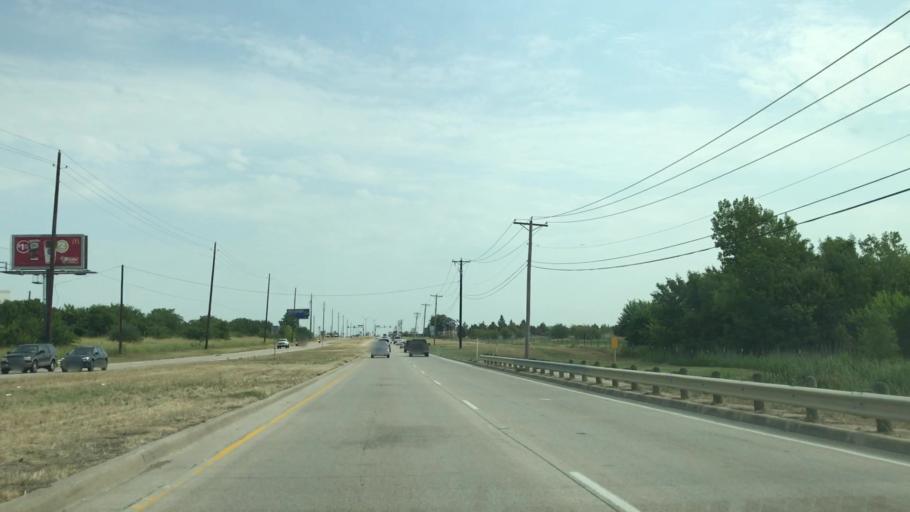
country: US
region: Texas
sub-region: Tarrant County
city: Keller
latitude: 32.9665
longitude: -97.2484
